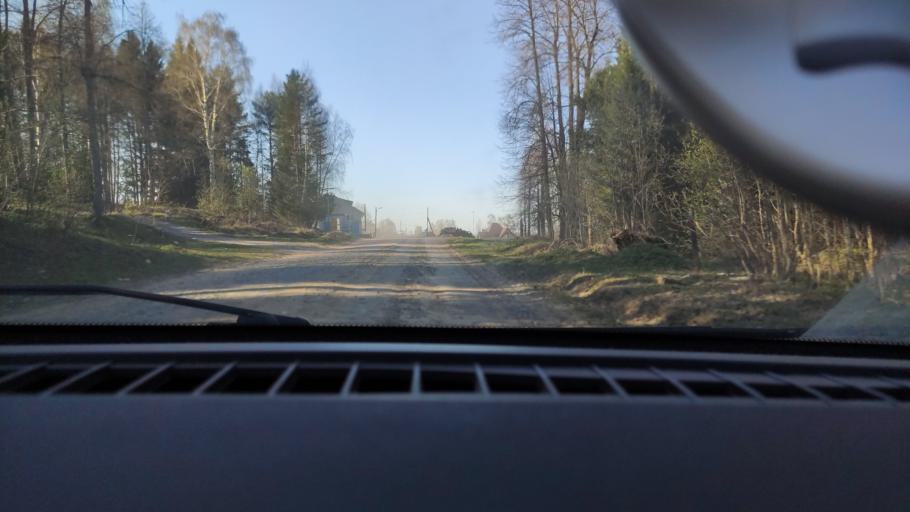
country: RU
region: Perm
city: Polazna
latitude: 58.1346
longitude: 56.4575
